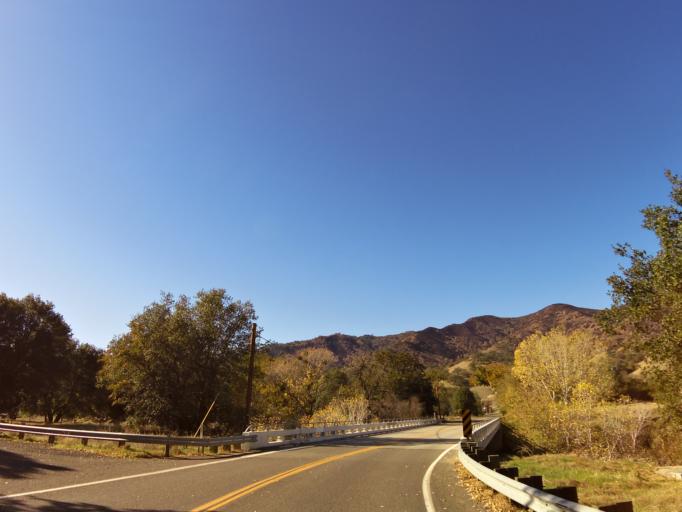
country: US
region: California
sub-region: Yolo County
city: Winters
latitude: 38.4675
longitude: -122.0467
